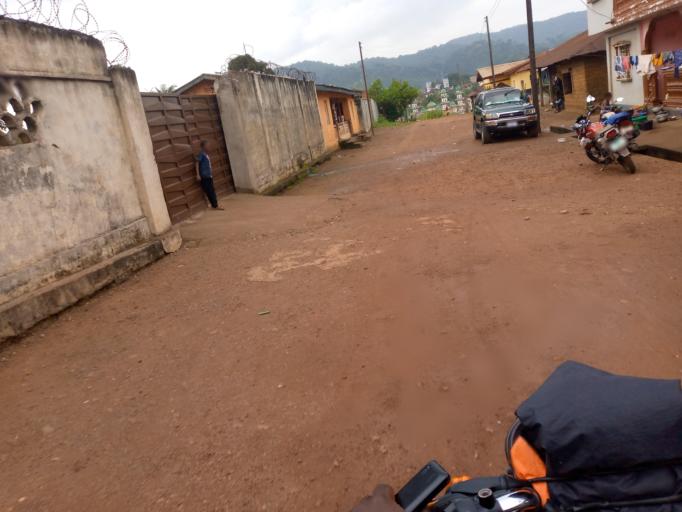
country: SL
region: Eastern Province
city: Kenema
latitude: 7.8672
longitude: -11.1879
